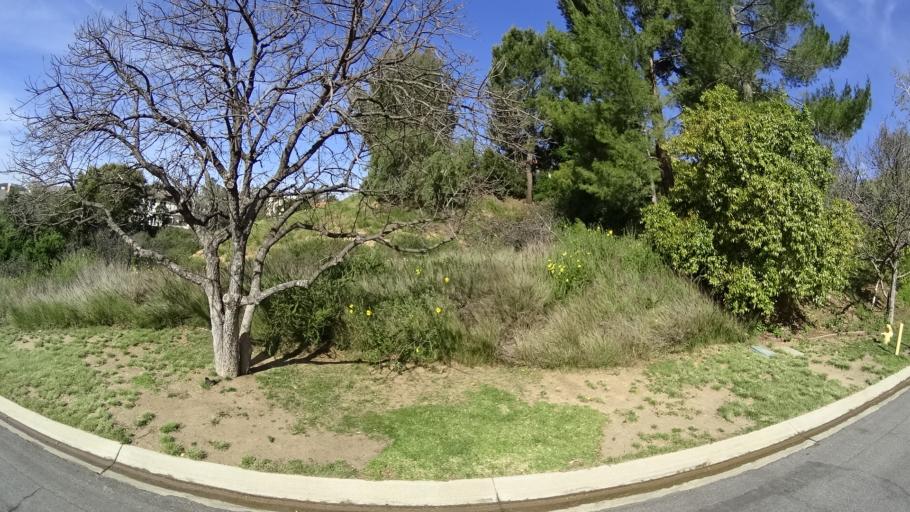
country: US
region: California
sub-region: Ventura County
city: Oak Park
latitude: 34.1968
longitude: -118.7881
